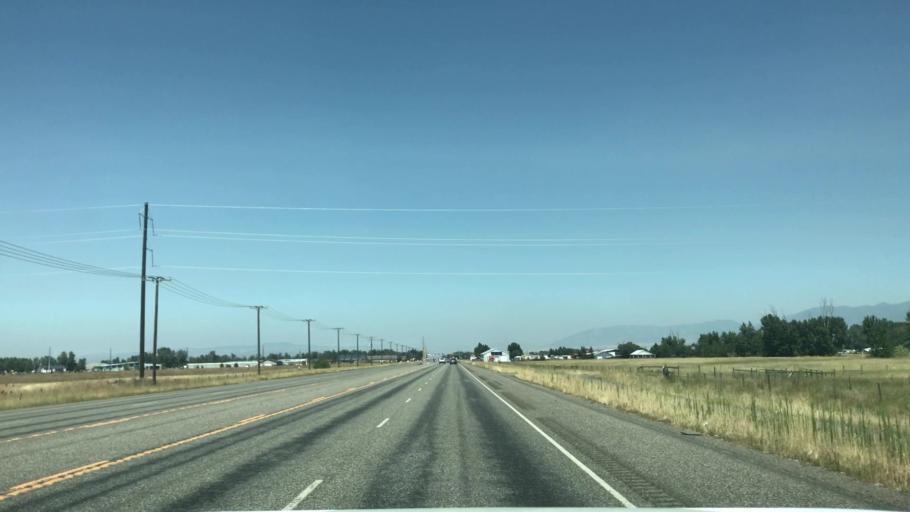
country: US
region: Montana
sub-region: Gallatin County
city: Four Corners
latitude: 45.6920
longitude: -111.1855
